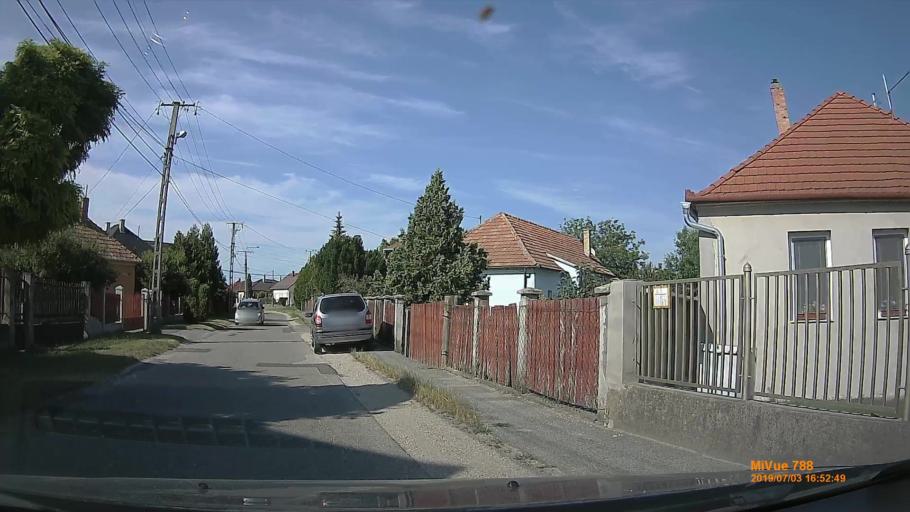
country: HU
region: Gyor-Moson-Sopron
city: Toltestava
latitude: 47.7048
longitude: 17.7363
